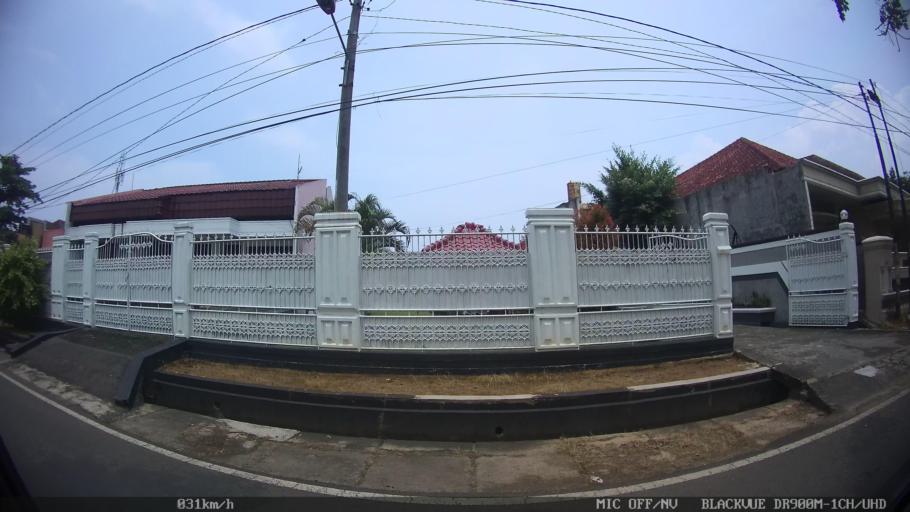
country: ID
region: Lampung
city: Bandarlampung
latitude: -5.4146
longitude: 105.2731
